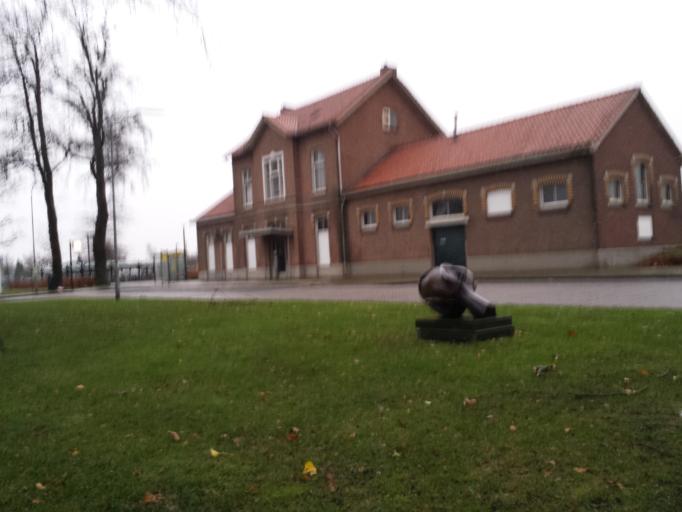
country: NL
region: Gelderland
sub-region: Gemeente Lochem
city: Almen
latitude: 52.1069
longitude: 6.3178
